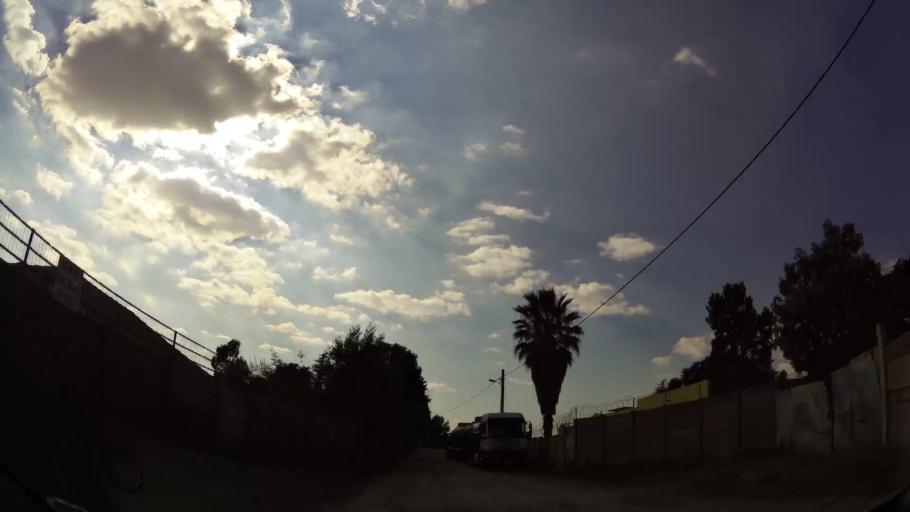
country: ZA
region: Gauteng
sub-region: Ekurhuleni Metropolitan Municipality
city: Benoni
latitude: -26.1027
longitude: 28.3633
